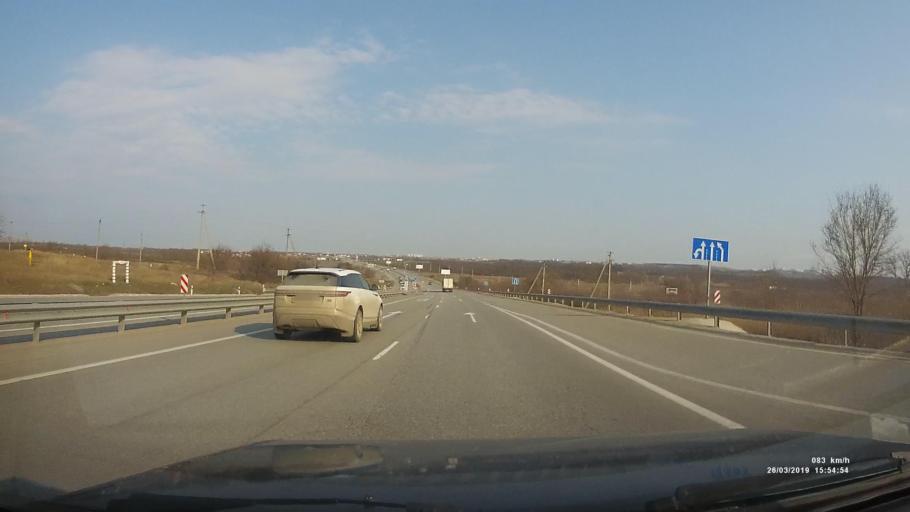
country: RU
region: Rostov
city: Kalinin
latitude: 47.2670
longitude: 39.5658
